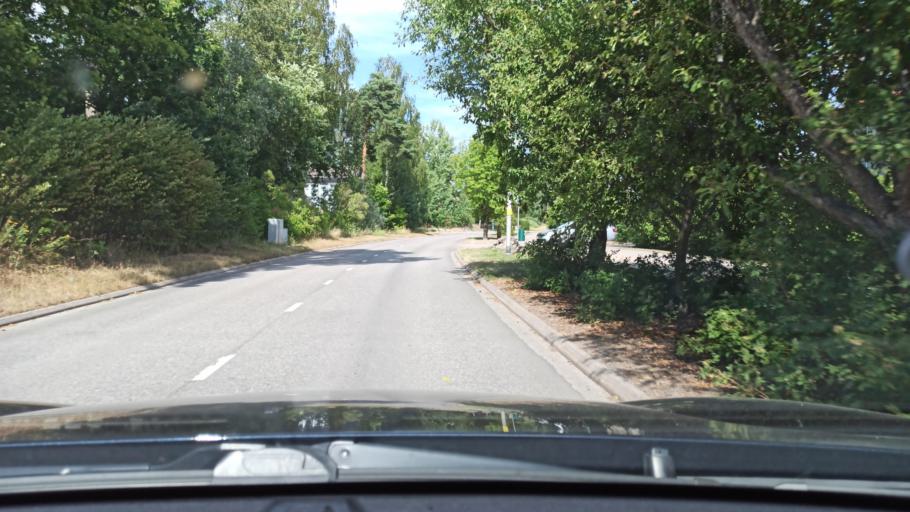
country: FI
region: Uusimaa
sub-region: Helsinki
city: Kirkkonummi
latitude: 60.1294
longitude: 24.4192
